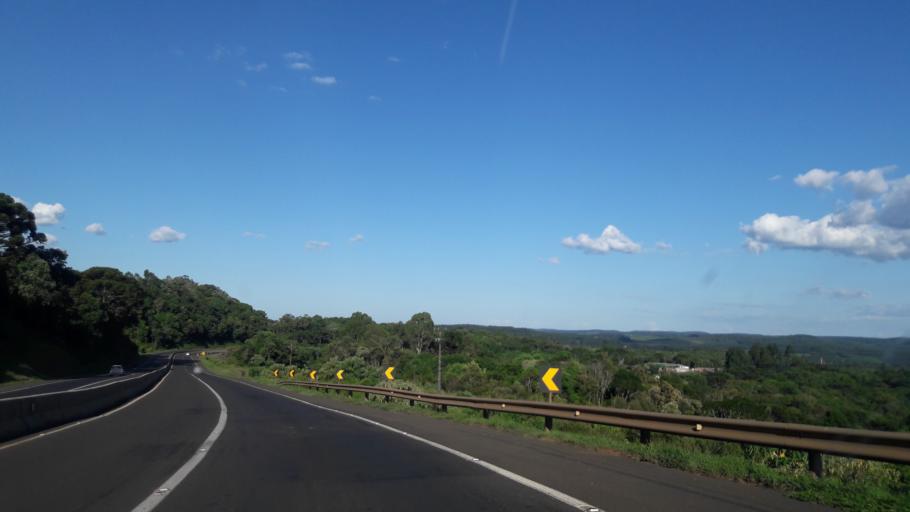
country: BR
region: Parana
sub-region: Guarapuava
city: Guarapuava
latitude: -25.3485
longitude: -51.3894
